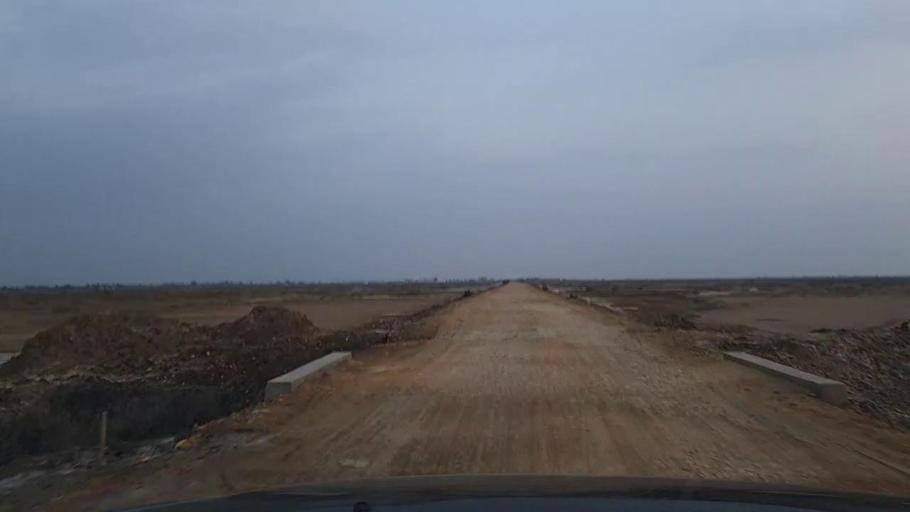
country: PK
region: Sindh
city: Jati
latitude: 24.4989
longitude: 68.3829
